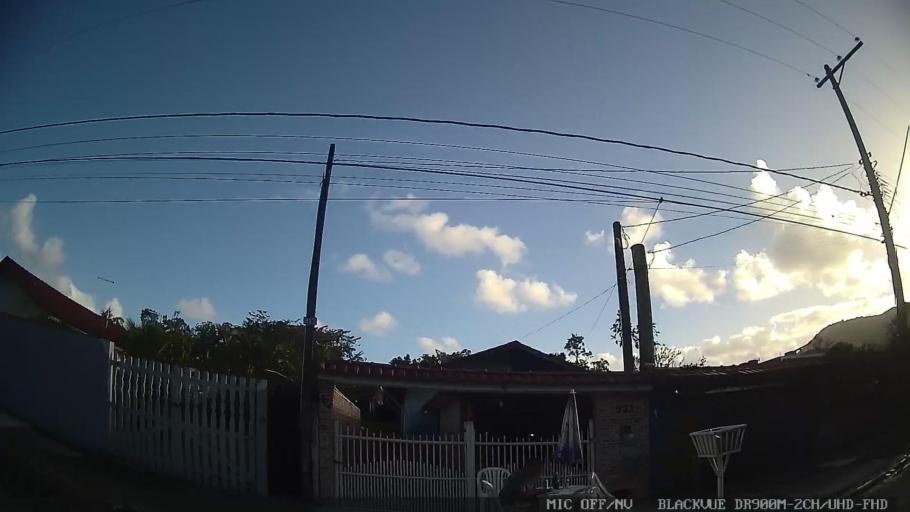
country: BR
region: Sao Paulo
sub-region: Itanhaem
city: Itanhaem
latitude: -24.1351
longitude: -46.7202
